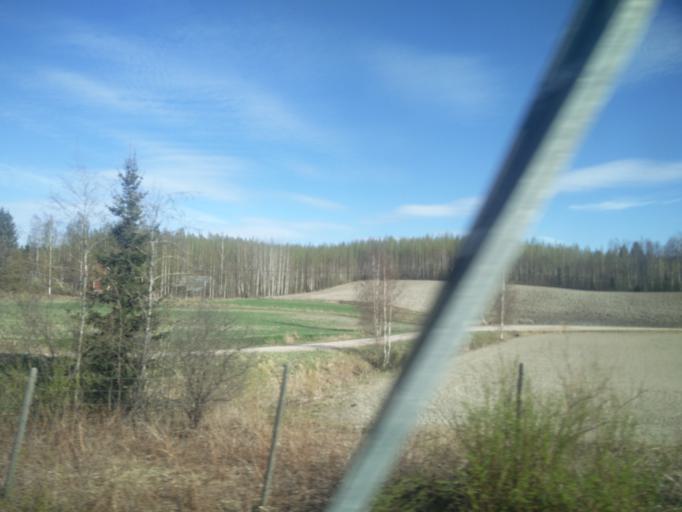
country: FI
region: Pirkanmaa
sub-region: Tampere
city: Kuhmalahti
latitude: 61.7156
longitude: 24.6452
